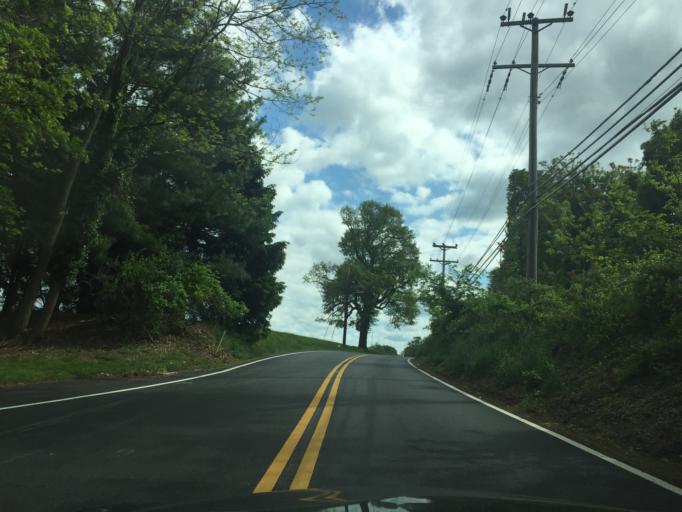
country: US
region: Maryland
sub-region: Baltimore County
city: Pikesville
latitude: 39.3866
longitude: -76.7042
